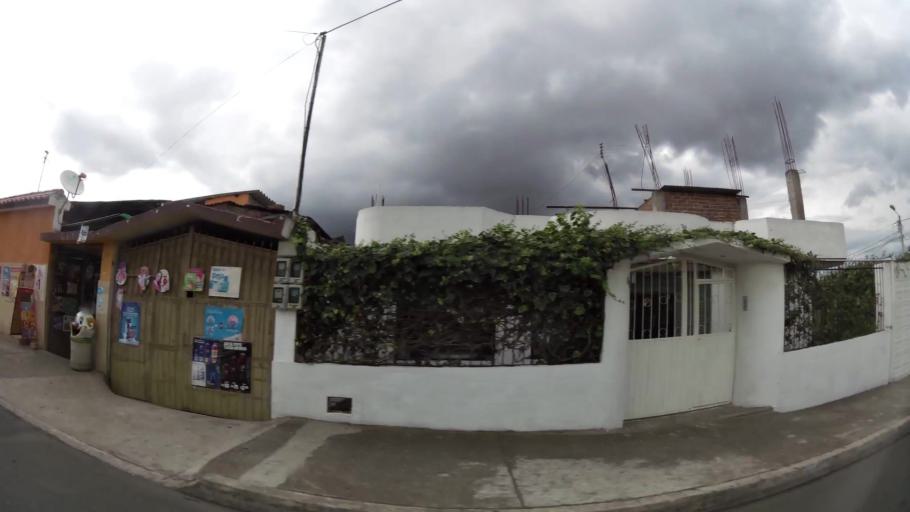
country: EC
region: Tungurahua
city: Ambato
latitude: -1.2661
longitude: -78.6198
